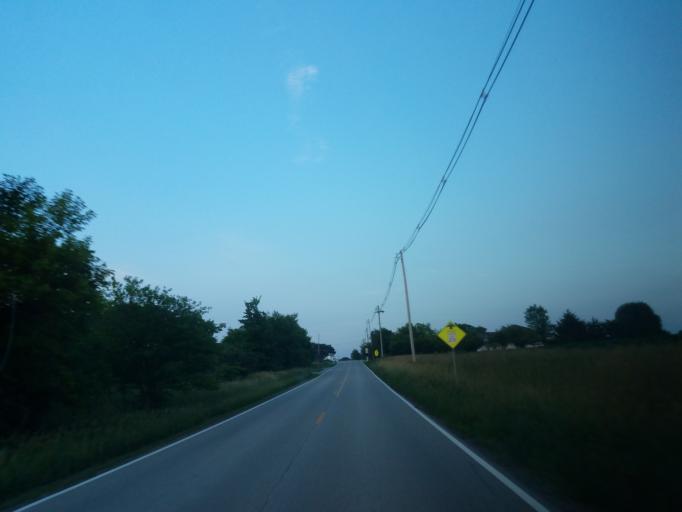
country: US
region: Illinois
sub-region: McLean County
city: Bloomington
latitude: 40.4415
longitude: -88.9969
